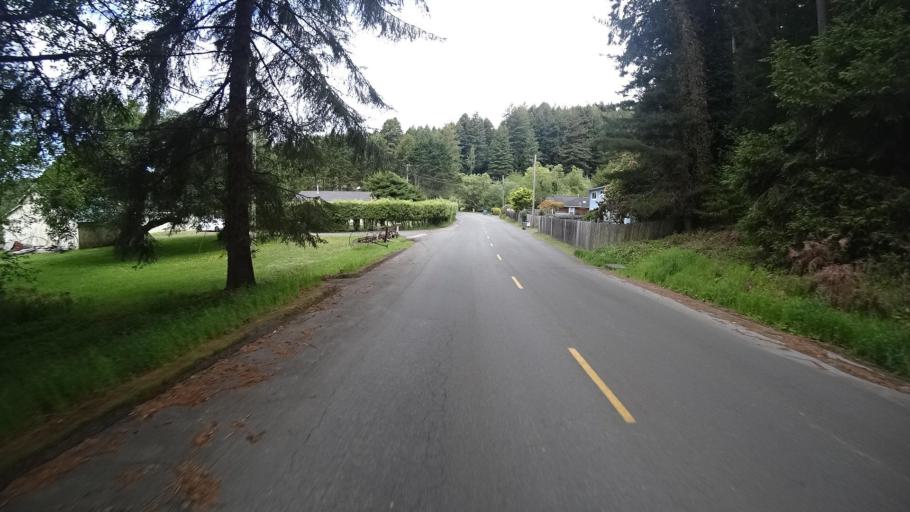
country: US
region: California
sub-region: Humboldt County
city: Bayside
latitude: 40.8556
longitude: -124.0569
